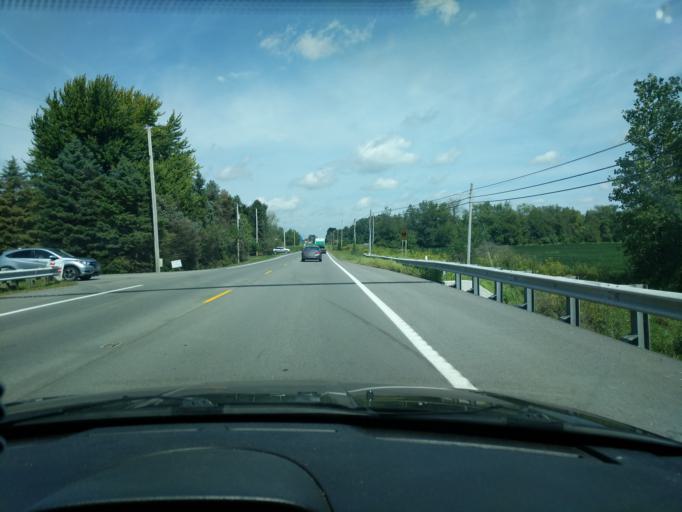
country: US
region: Ohio
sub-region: Logan County
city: Bellefontaine
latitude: 40.3174
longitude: -83.7604
